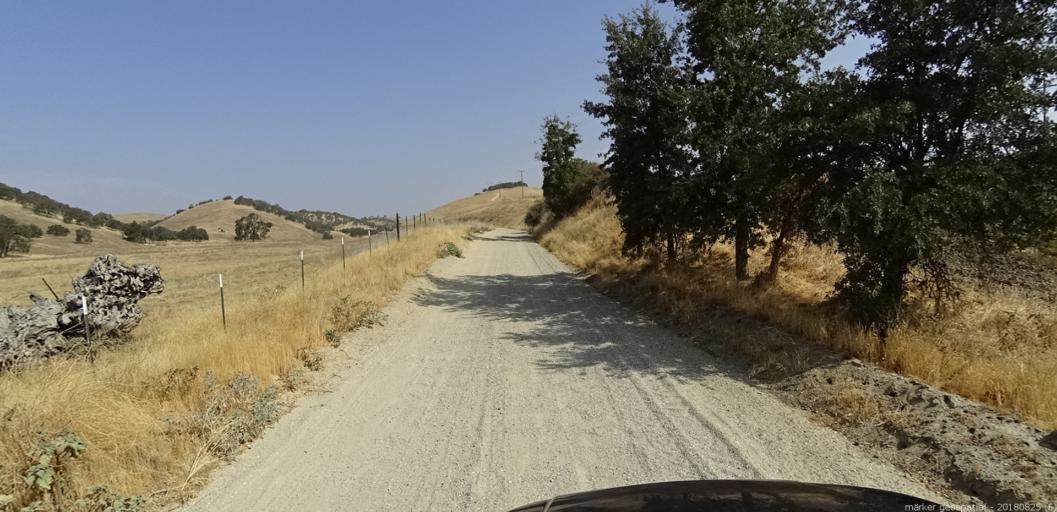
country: US
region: California
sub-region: San Luis Obispo County
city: San Miguel
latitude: 35.8363
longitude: -120.6553
